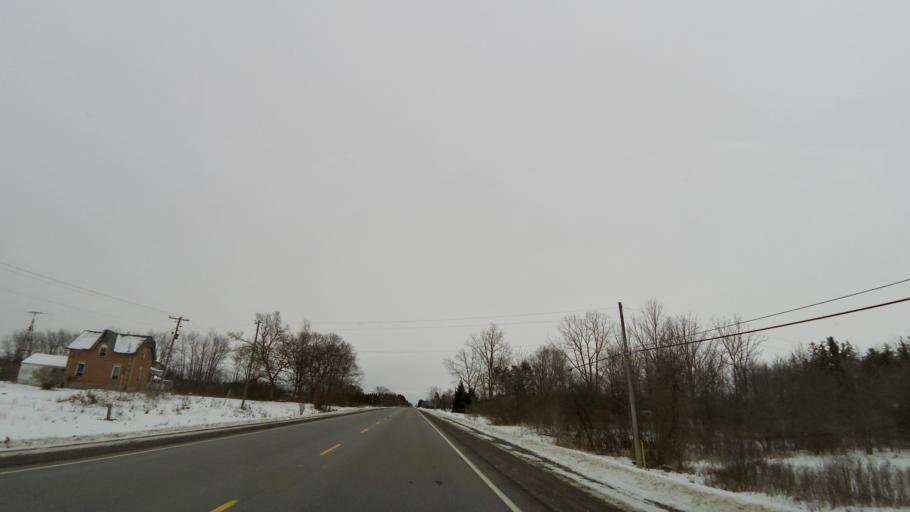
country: CA
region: Ontario
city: Cambridge
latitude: 43.3110
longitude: -80.1573
